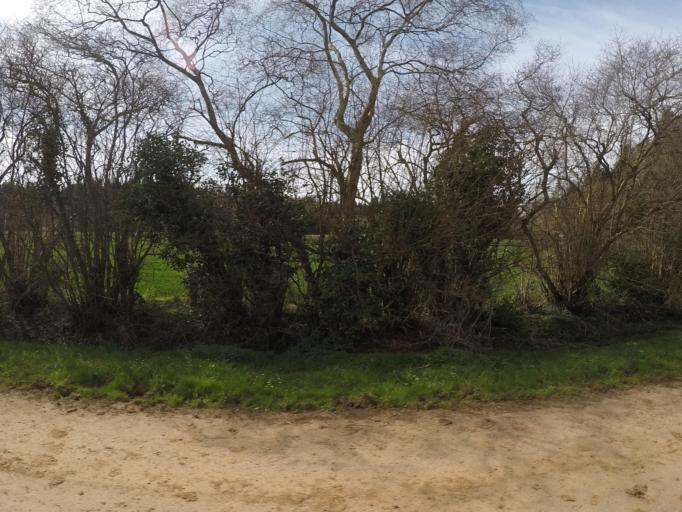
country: FR
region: Brittany
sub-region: Departement des Cotes-d'Armor
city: Plelo
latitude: 48.5841
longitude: -2.9339
